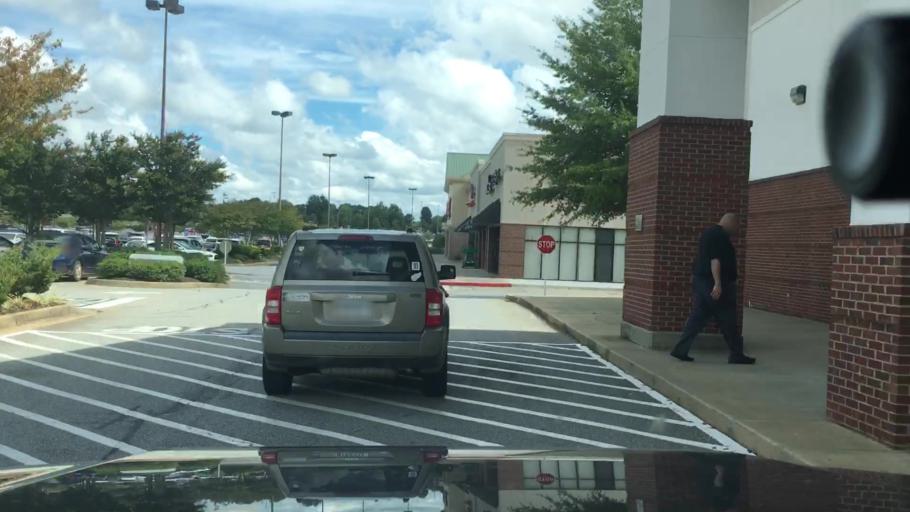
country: US
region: Georgia
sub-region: Coweta County
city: Newnan
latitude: 33.3921
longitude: -84.7594
